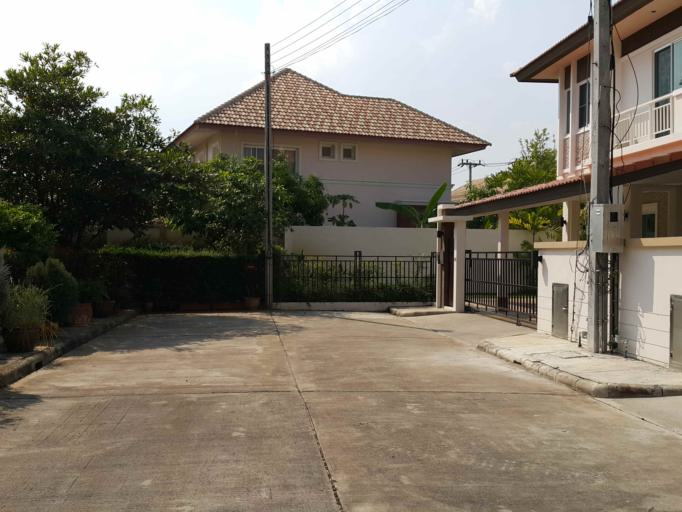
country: TH
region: Chiang Mai
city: Saraphi
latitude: 18.7558
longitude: 99.0404
